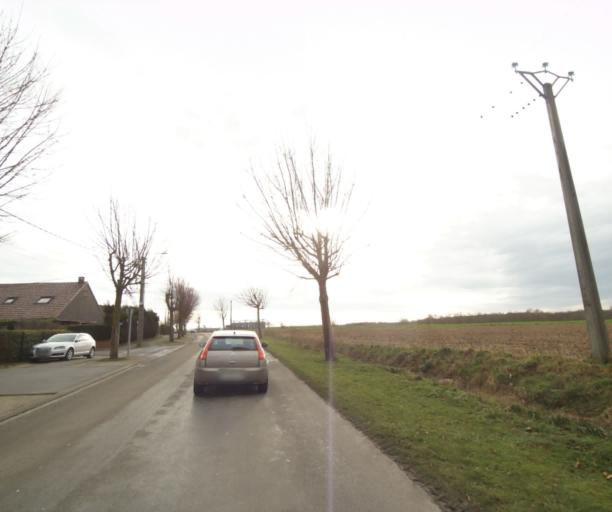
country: FR
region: Nord-Pas-de-Calais
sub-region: Departement du Nord
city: Quarouble
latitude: 50.3822
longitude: 3.6231
